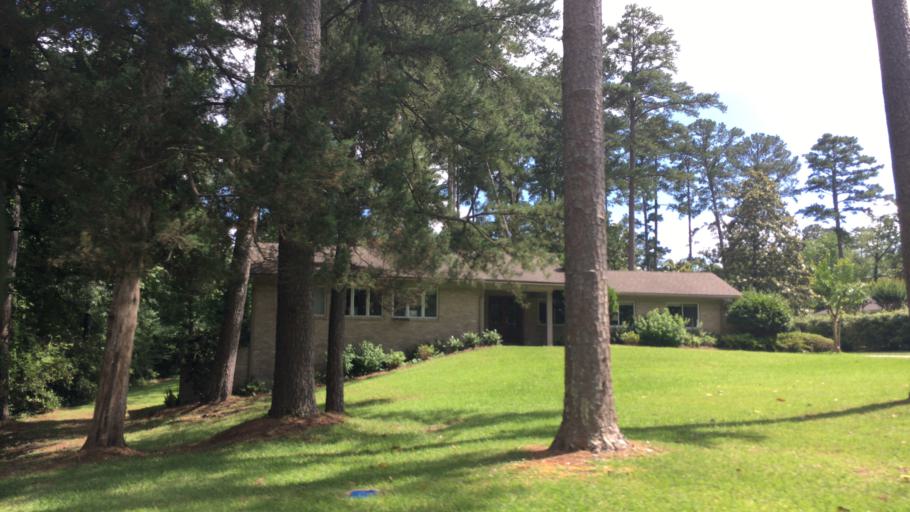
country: US
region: Louisiana
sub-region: Lincoln Parish
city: Ruston
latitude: 32.5503
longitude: -92.6328
